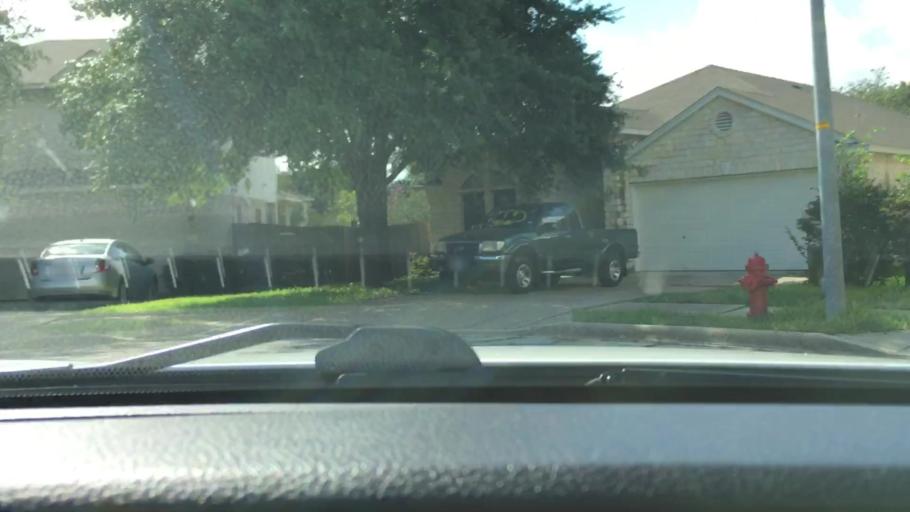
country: US
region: Texas
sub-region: Travis County
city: Windemere
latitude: 30.4747
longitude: -97.6490
